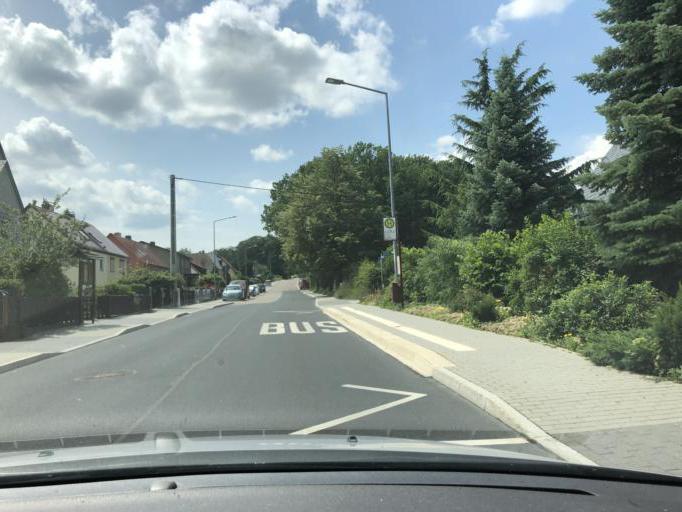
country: DE
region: Saxony
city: Freital
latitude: 50.9984
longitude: 13.6788
